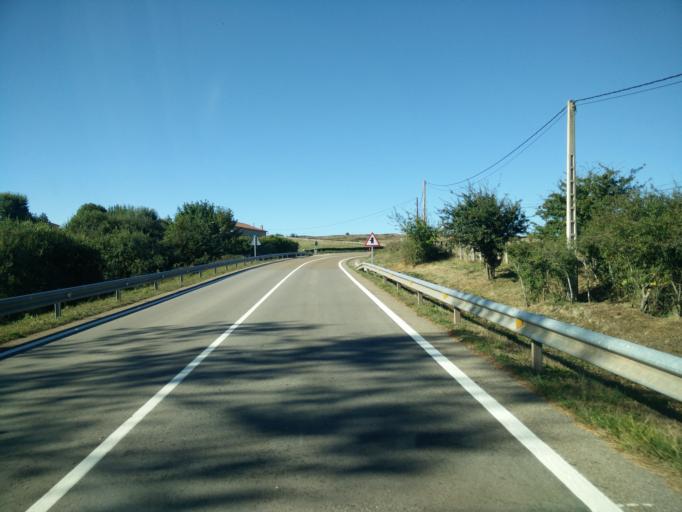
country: ES
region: Castille and Leon
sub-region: Provincia de Burgos
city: Arija
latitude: 43.0263
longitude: -3.9593
